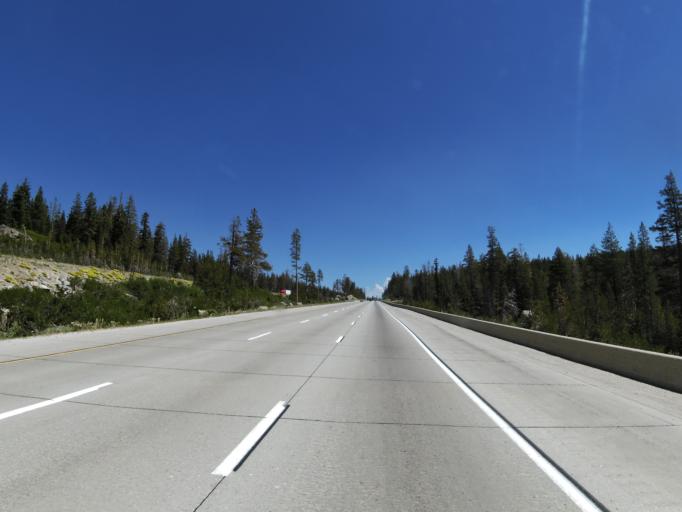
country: US
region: California
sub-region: Nevada County
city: Truckee
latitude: 39.3282
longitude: -120.3689
